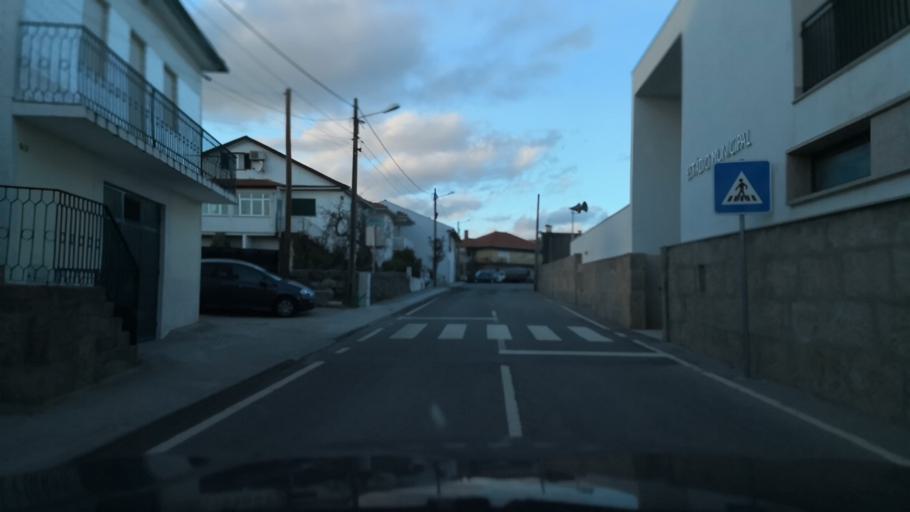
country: PT
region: Braganca
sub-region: Carrazeda de Ansiaes
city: Carrazeda de Anciaes
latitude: 41.2380
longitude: -7.3066
